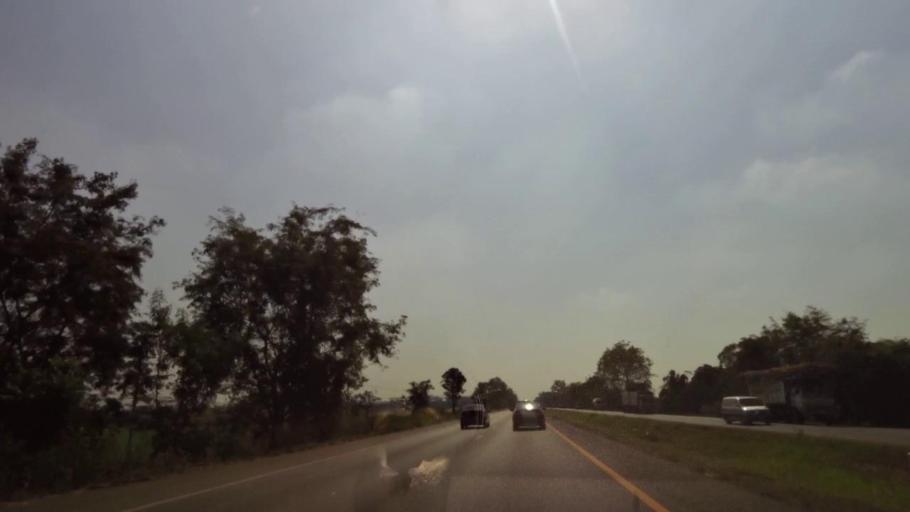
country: TH
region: Phichit
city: Wachira Barami
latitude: 16.4476
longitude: 100.1463
